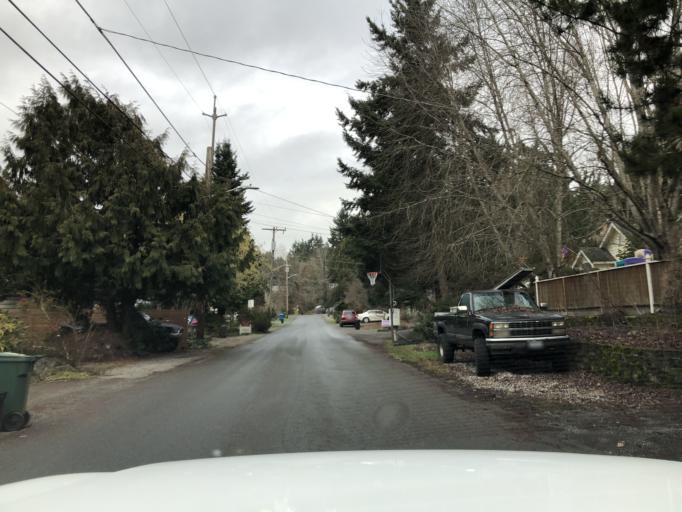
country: US
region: Washington
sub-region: King County
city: Inglewood-Finn Hill
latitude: 47.7021
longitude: -122.2801
